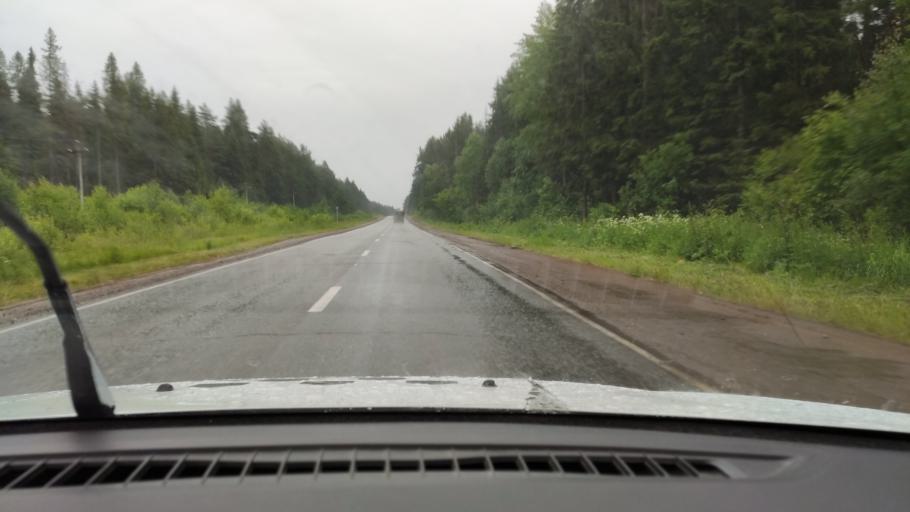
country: RU
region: Udmurtiya
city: Votkinsk
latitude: 57.0784
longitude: 54.0261
